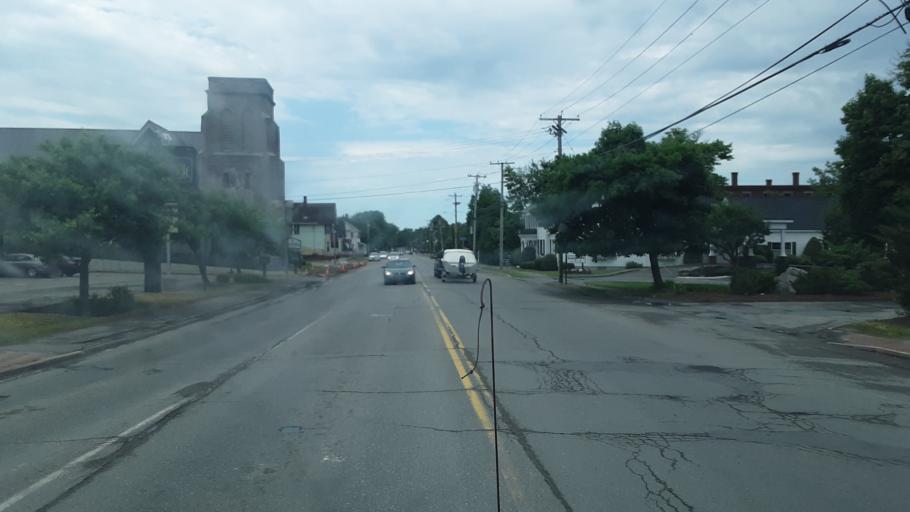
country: US
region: Maine
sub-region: Penobscot County
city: Brewer
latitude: 44.7947
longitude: -68.7662
